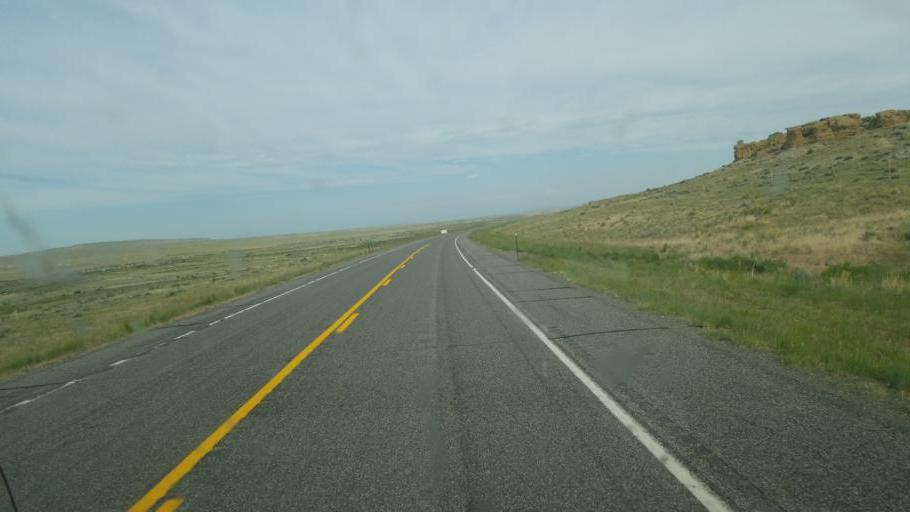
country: US
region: Wyoming
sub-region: Fremont County
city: Riverton
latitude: 43.2207
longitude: -108.0059
